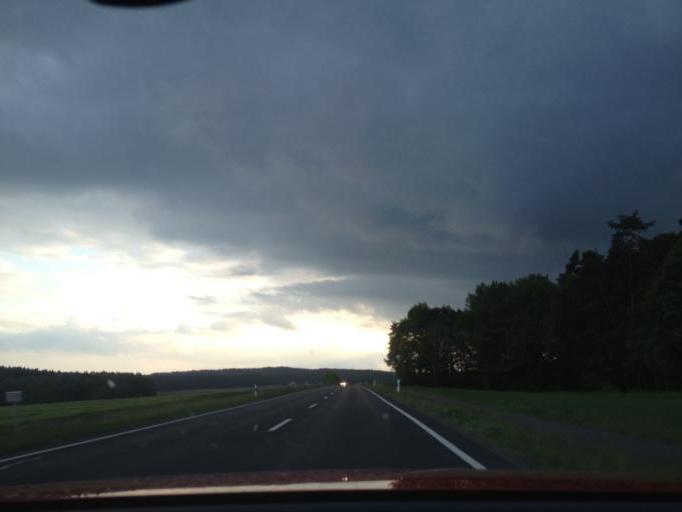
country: DE
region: Bavaria
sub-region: Upper Palatinate
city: Hahnbach
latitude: 49.5309
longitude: 11.7743
